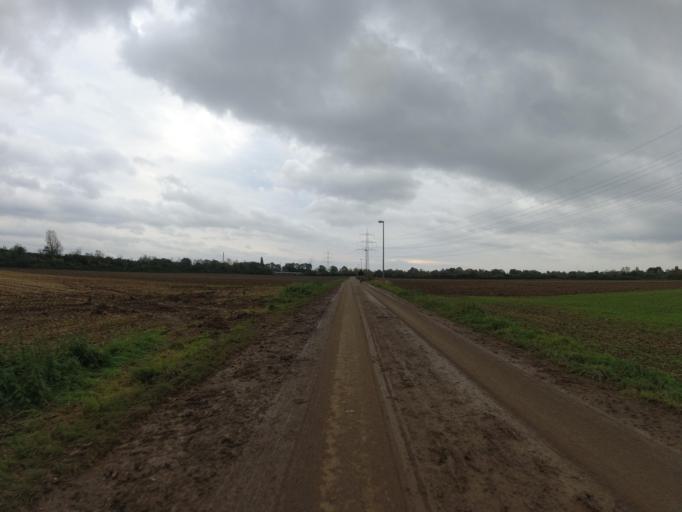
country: DE
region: North Rhine-Westphalia
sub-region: Regierungsbezirk Dusseldorf
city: Hochfeld
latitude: 51.3912
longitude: 6.6897
